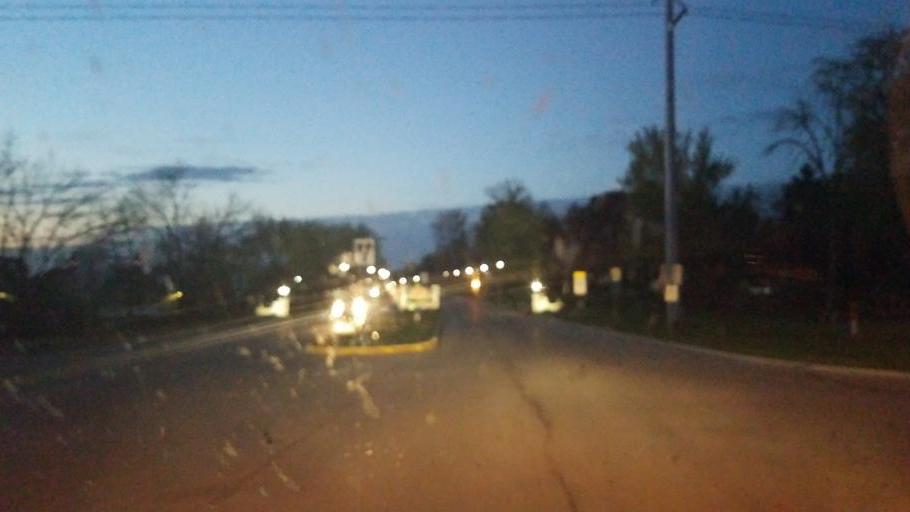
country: US
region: Wisconsin
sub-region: Waukesha County
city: Delafield
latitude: 43.0554
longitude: -88.4045
